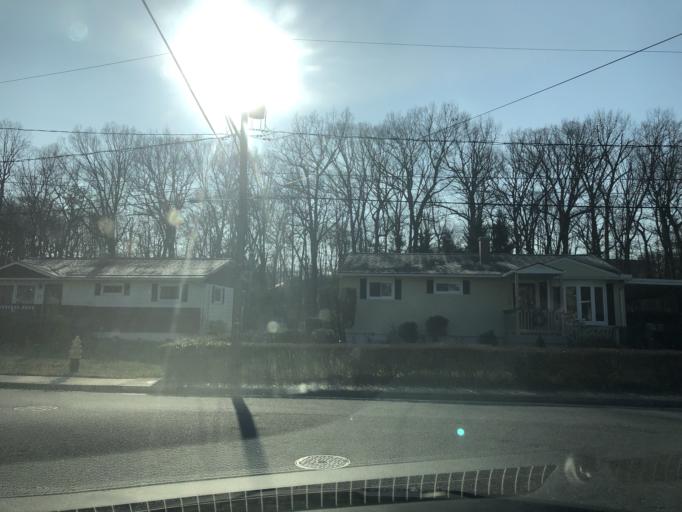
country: US
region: Maryland
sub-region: Anne Arundel County
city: Odenton
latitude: 39.0732
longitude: -76.7009
